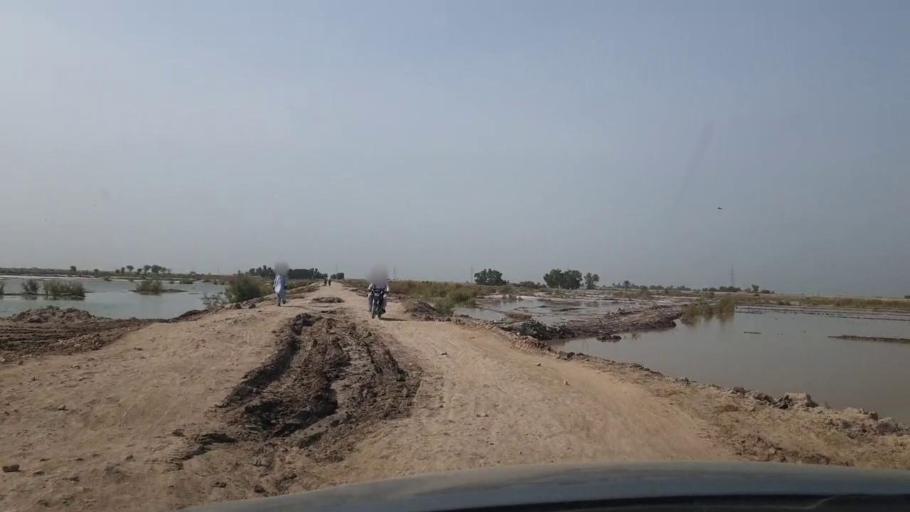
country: PK
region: Sindh
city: Lakhi
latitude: 27.8390
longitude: 68.6997
